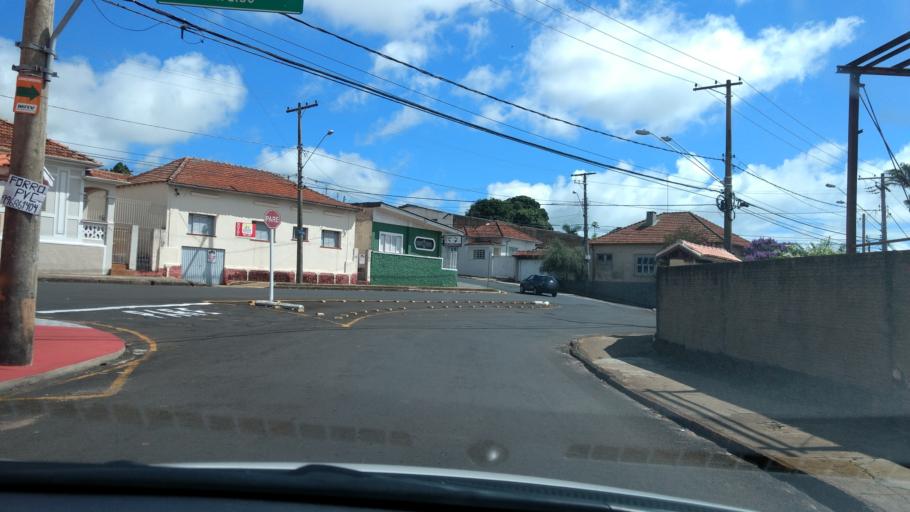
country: BR
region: Sao Paulo
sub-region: Botucatu
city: Botucatu
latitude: -22.8717
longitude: -48.4447
